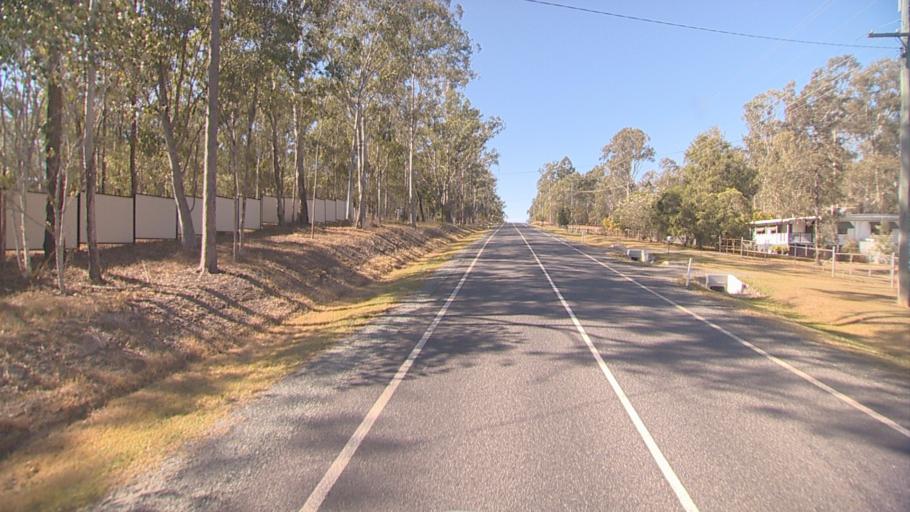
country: AU
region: Queensland
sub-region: Logan
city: Cedar Vale
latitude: -27.8525
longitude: 153.0290
